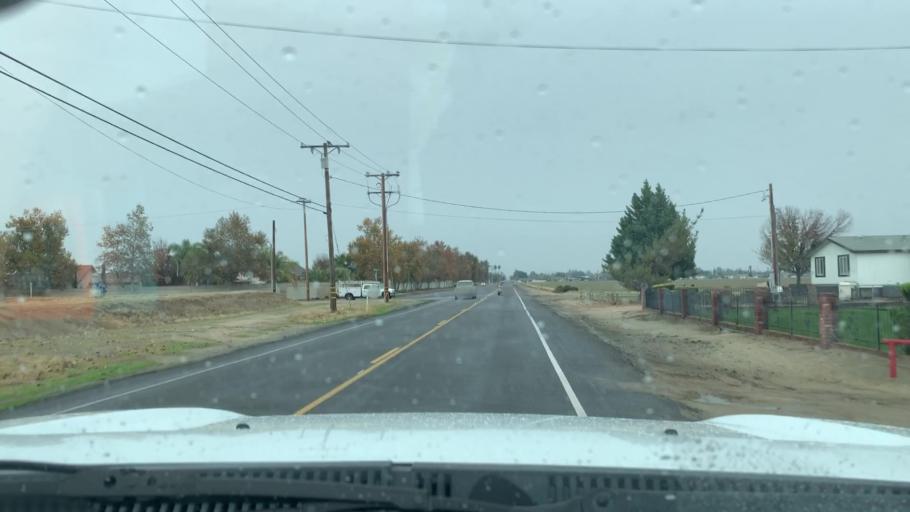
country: US
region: California
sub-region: Kern County
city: Delano
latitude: 35.7614
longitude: -119.2682
